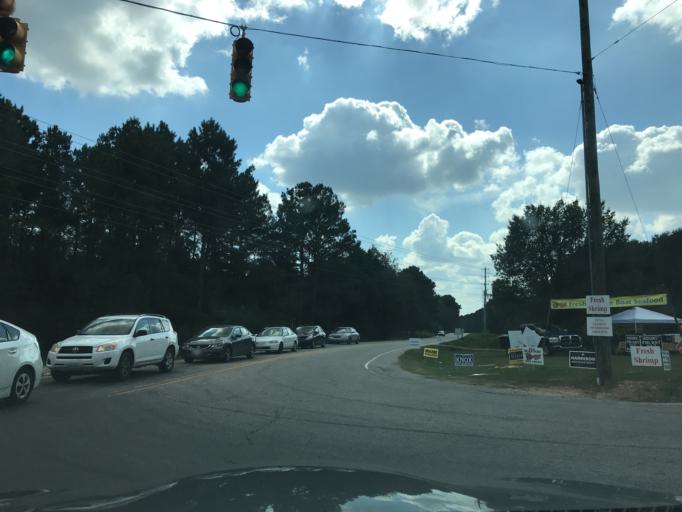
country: US
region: North Carolina
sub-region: Wake County
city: Wake Forest
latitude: 35.9199
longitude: -78.5239
